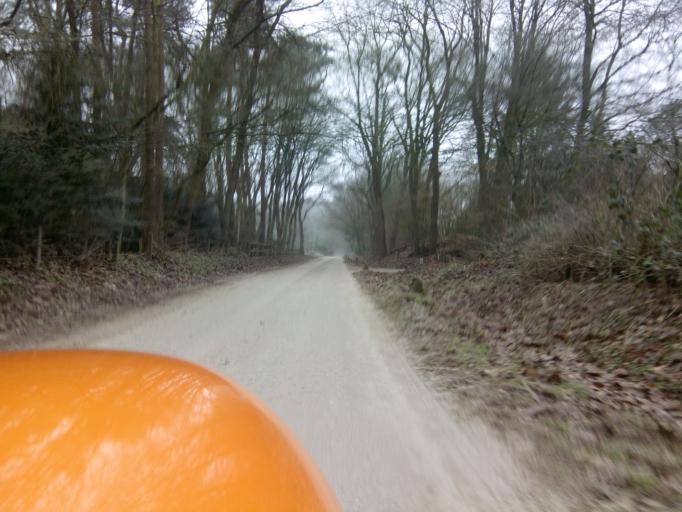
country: NL
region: Gelderland
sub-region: Gemeente Barneveld
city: Garderen
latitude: 52.2216
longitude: 5.6897
